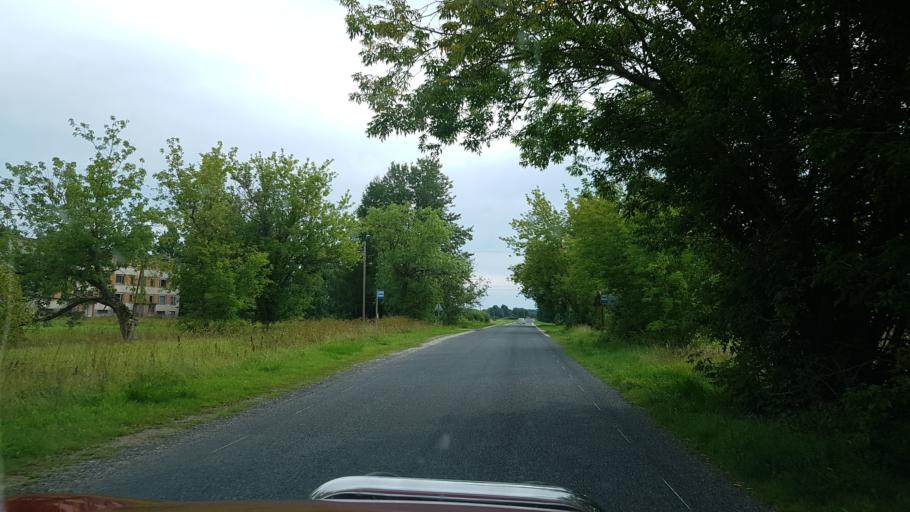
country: EE
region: Laeaene
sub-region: Lihula vald
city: Lihula
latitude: 58.8866
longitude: 23.8680
